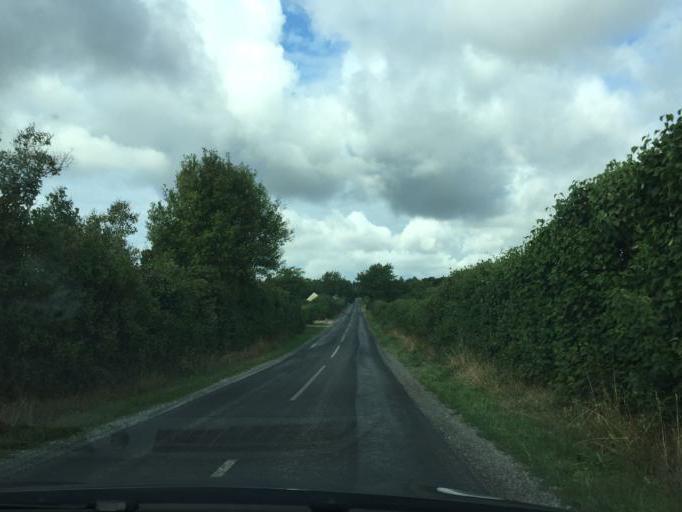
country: DK
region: South Denmark
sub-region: Assens Kommune
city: Harby
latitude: 55.1938
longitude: 10.2169
